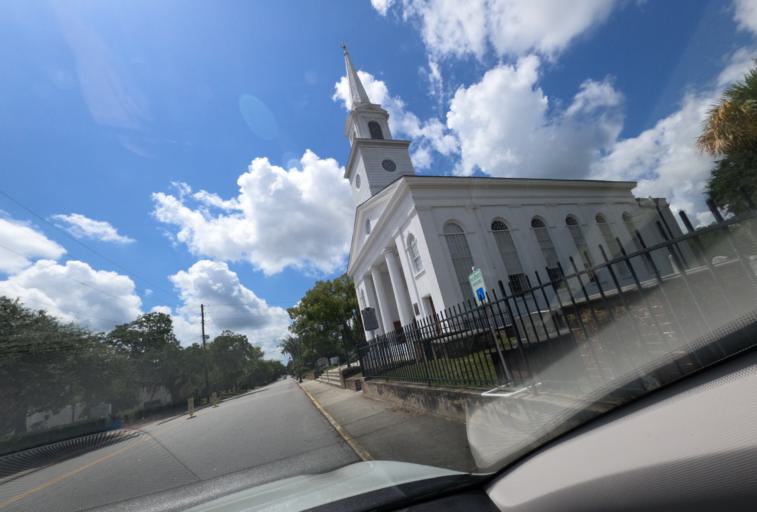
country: US
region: South Carolina
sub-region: Beaufort County
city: Beaufort
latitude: 32.4350
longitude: -80.6729
